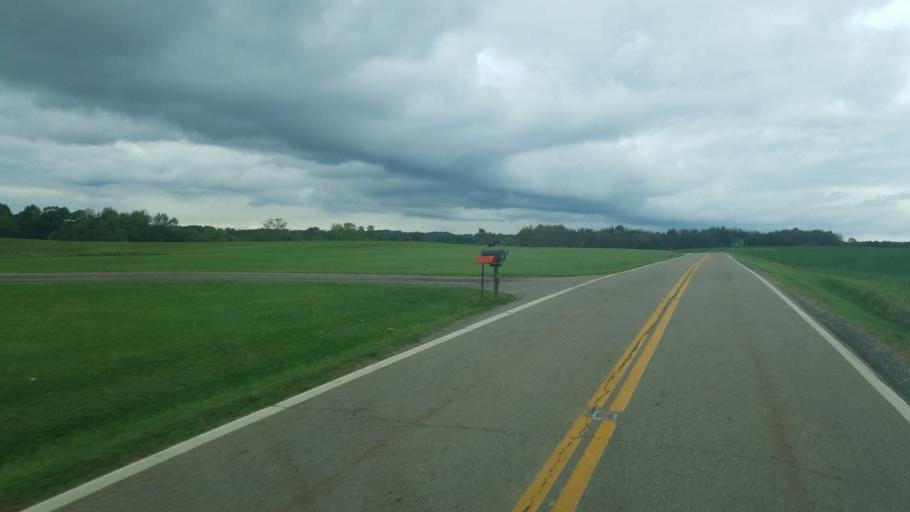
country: US
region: Ohio
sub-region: Ashland County
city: Loudonville
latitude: 40.5330
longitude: -82.1558
